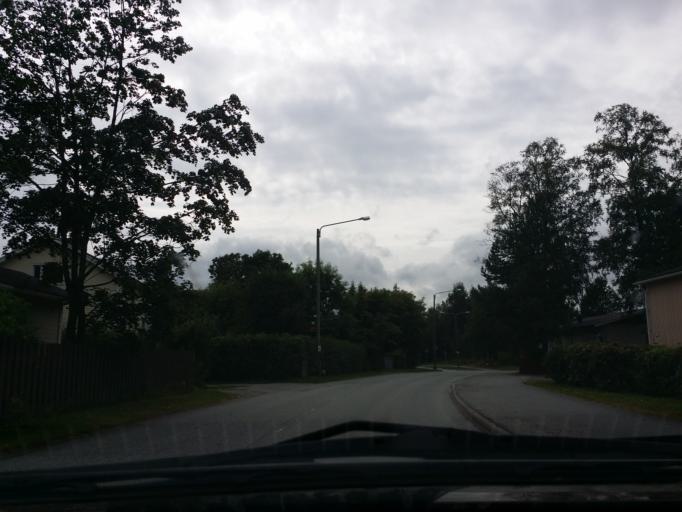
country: FI
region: Satakunta
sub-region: Pori
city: Pori
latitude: 61.5045
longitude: 21.8043
